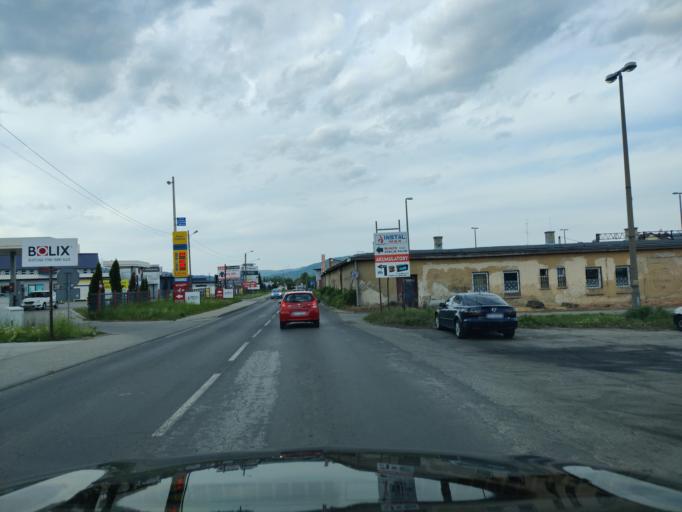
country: PL
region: Silesian Voivodeship
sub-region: Powiat zywiecki
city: Zywiec
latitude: 49.6806
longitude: 19.1855
